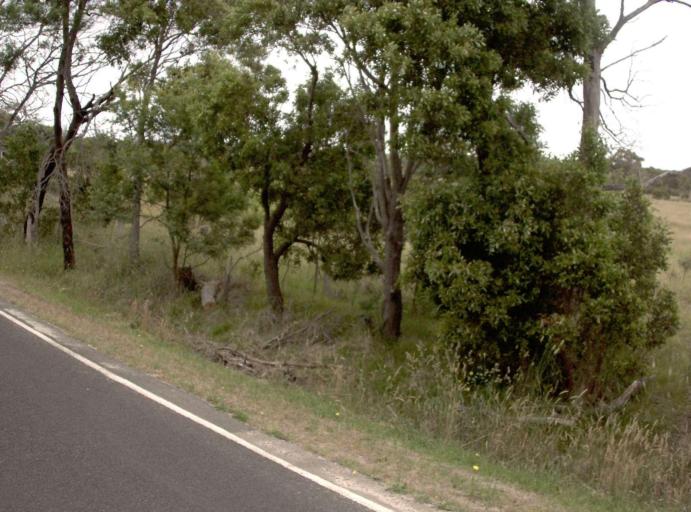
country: AU
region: Victoria
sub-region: Latrobe
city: Traralgon
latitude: -38.4887
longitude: 146.8196
